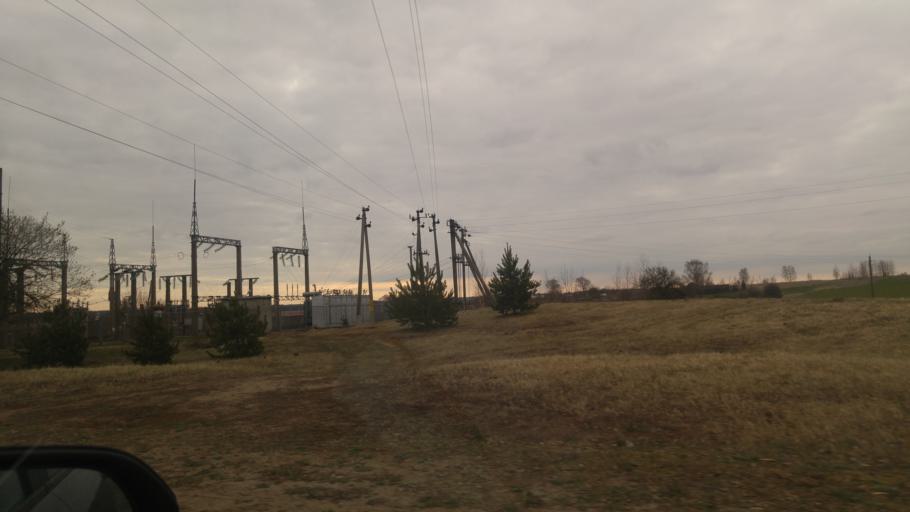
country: BY
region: Minsk
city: Pukhavichy
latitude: 53.7017
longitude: 28.2296
